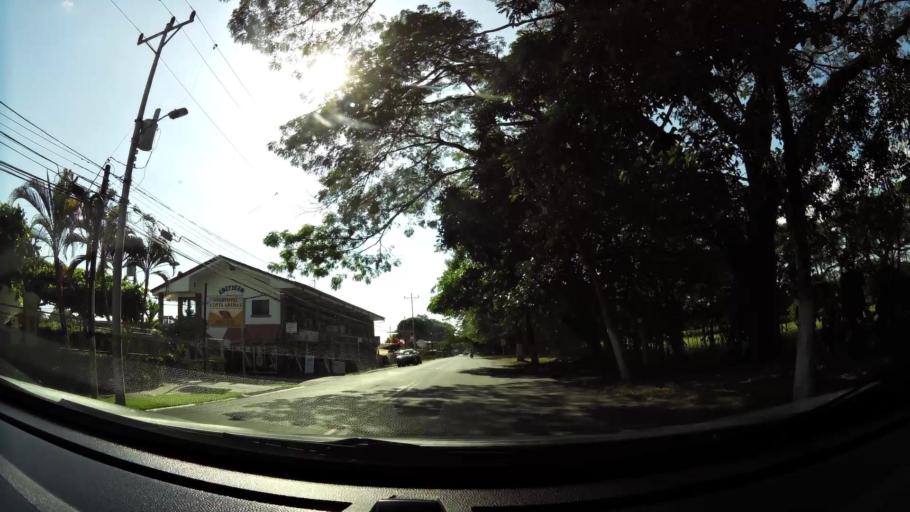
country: CR
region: Puntarenas
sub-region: Canton de Garabito
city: Jaco
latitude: 9.6112
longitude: -84.6194
